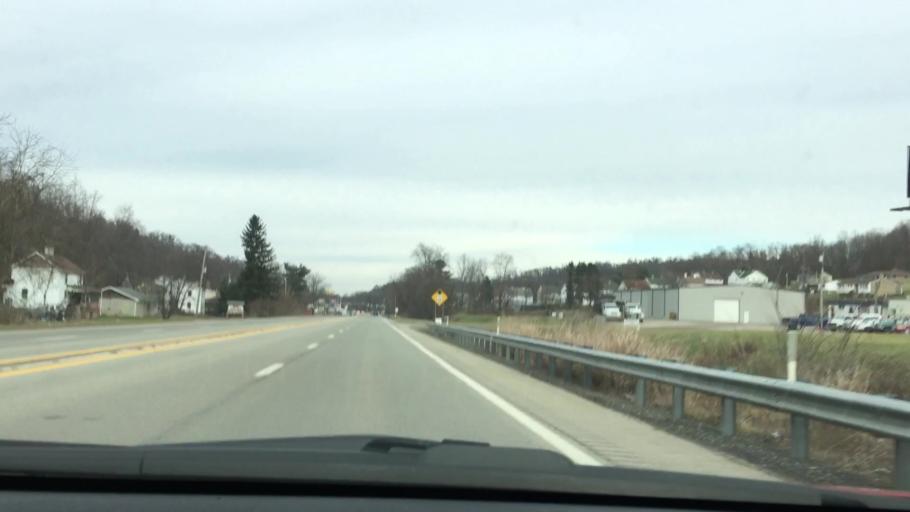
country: US
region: Pennsylvania
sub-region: Fayette County
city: Perryopolis
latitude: 40.0586
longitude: -79.7668
